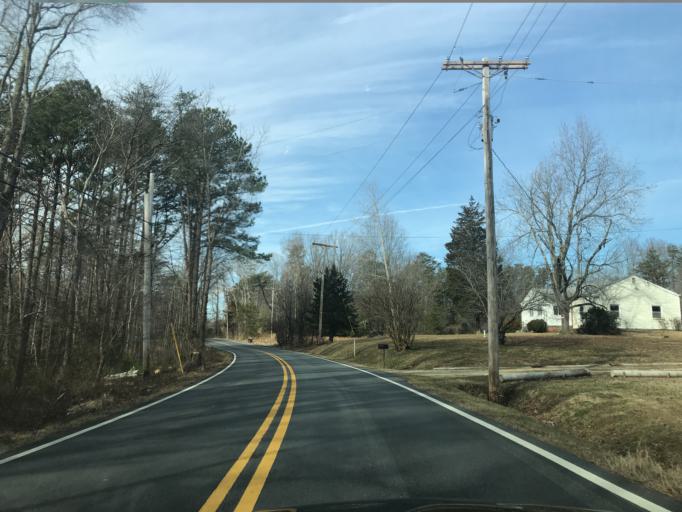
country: US
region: Maryland
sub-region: Charles County
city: Indian Head
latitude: 38.4935
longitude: -77.1674
